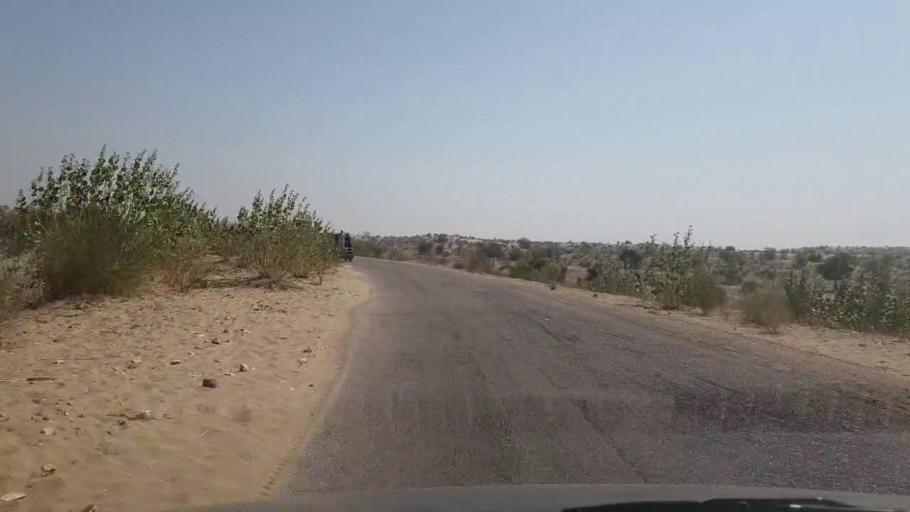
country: PK
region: Sindh
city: Chor
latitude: 25.5988
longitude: 70.0079
